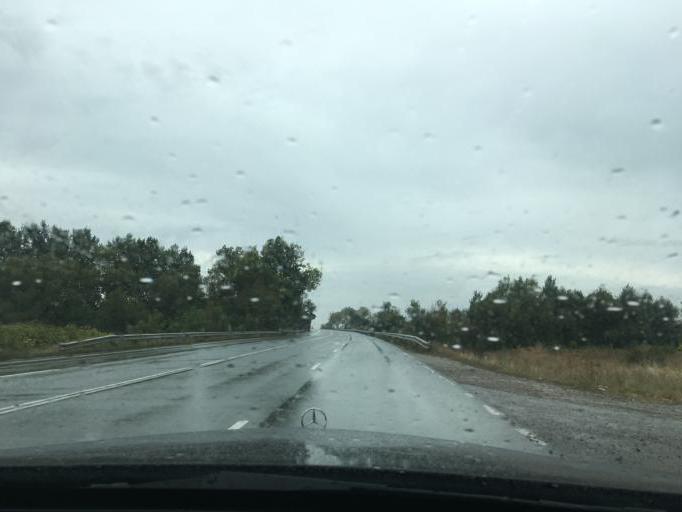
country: BG
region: Sofiya
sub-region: Obshtina Bozhurishte
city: Bozhurishte
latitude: 42.7913
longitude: 23.1518
